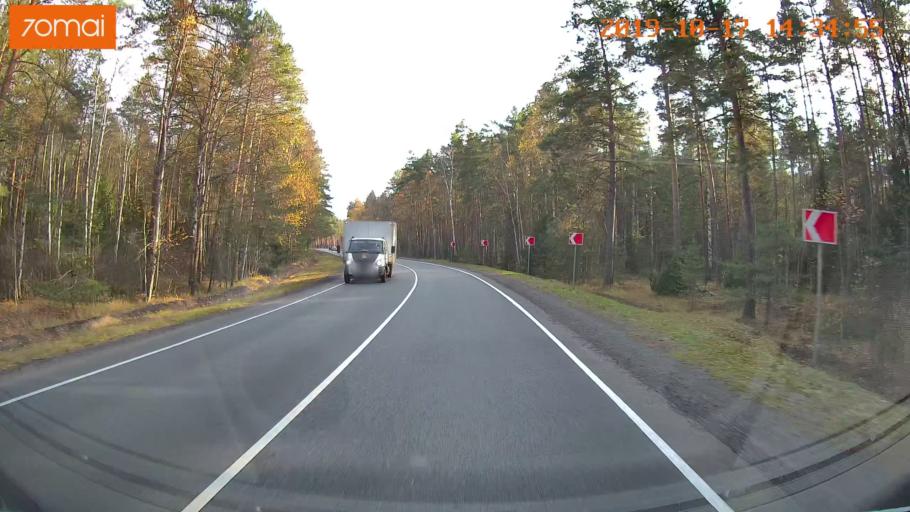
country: RU
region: Rjazan
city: Solotcha
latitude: 54.9059
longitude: 40.0004
